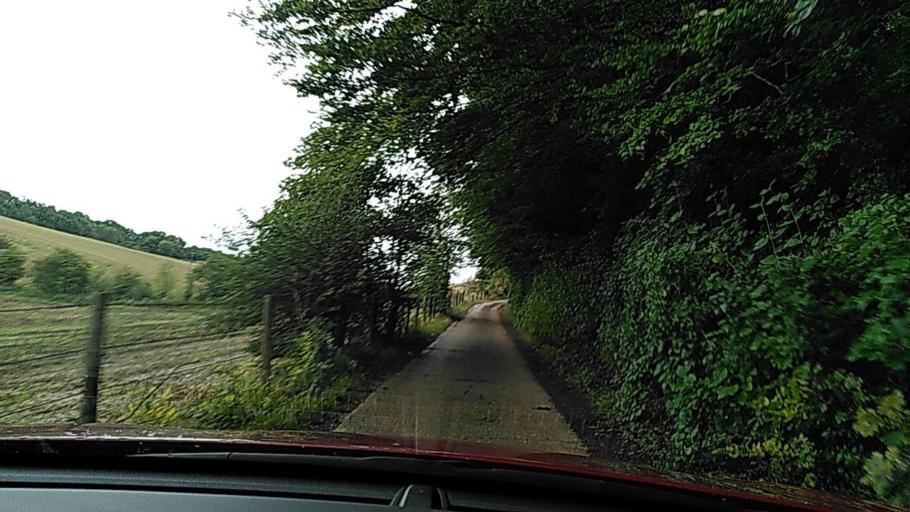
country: GB
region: England
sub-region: West Berkshire
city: Tilehurst
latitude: 51.4805
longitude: -1.0152
